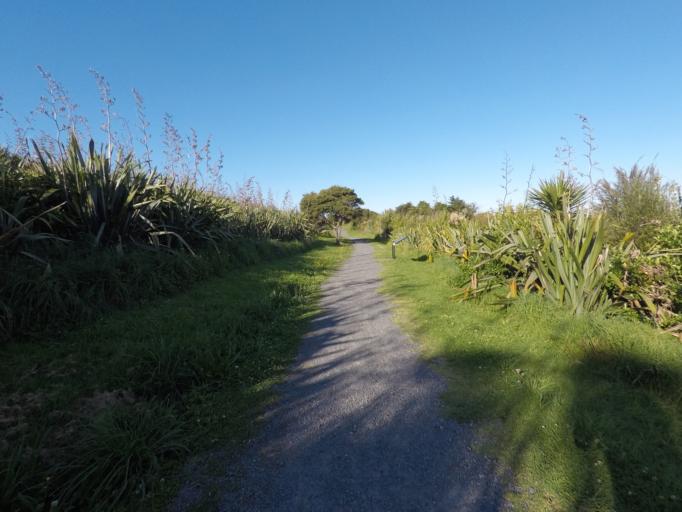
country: NZ
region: Auckland
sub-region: Auckland
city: Rosebank
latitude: -36.8418
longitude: 174.6583
